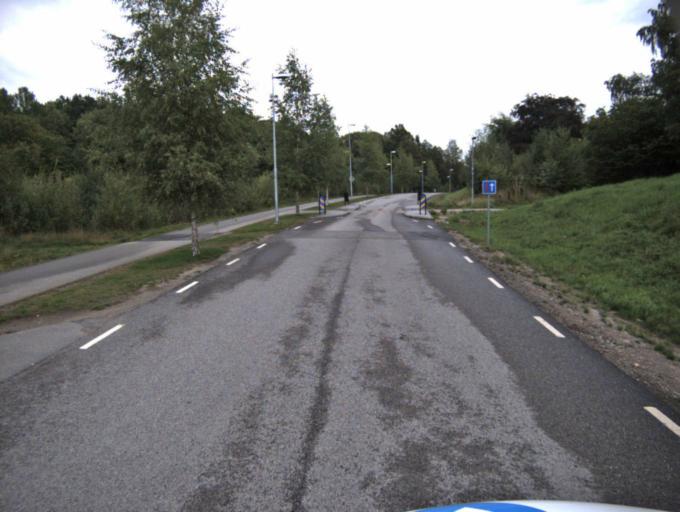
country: SE
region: Vaestra Goetaland
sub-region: Ulricehamns Kommun
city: Ulricehamn
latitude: 57.7884
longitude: 13.4280
